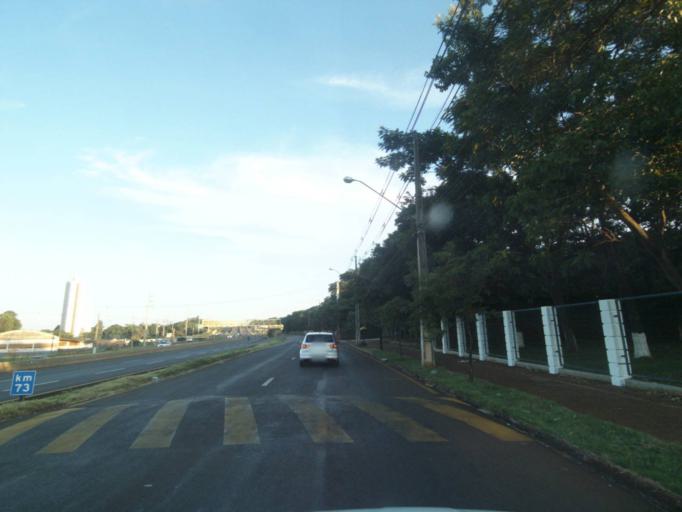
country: BR
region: Parana
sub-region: Londrina
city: Londrina
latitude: -23.3441
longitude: -51.1792
